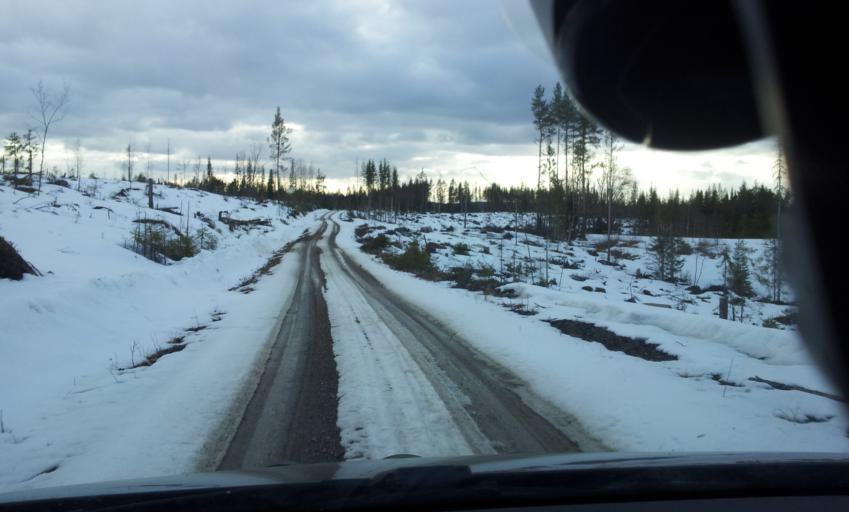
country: SE
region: Vaesternorrland
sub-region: Ange Kommun
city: Ange
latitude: 62.1922
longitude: 15.7157
